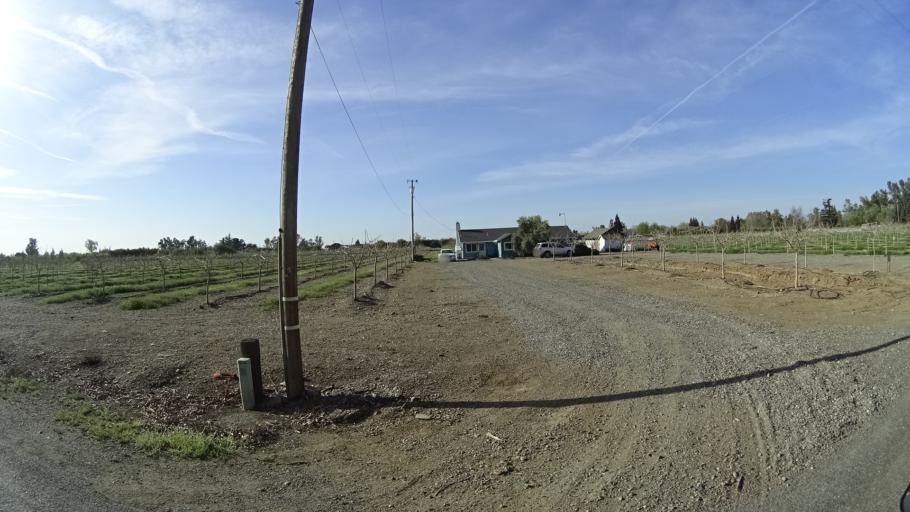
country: US
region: California
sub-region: Glenn County
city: Orland
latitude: 39.7153
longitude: -122.2131
